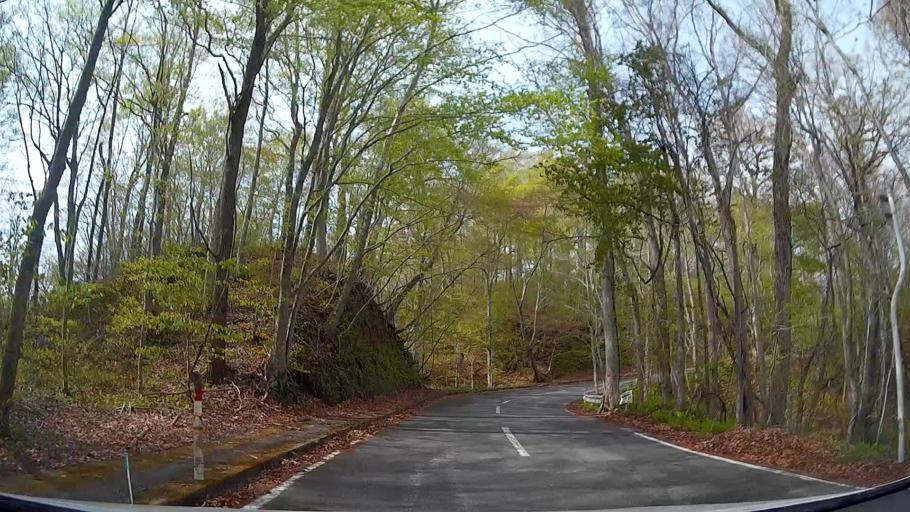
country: JP
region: Akita
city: Hanawa
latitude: 40.4367
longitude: 140.9164
